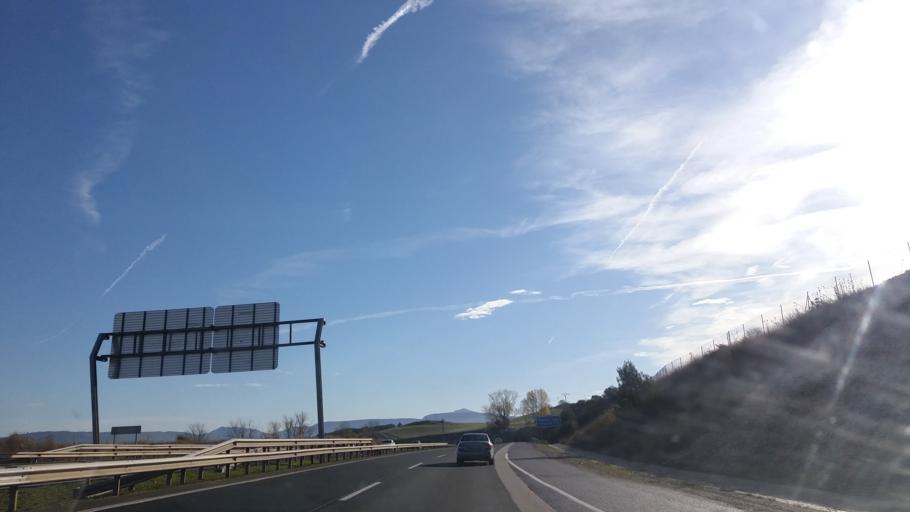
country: ES
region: Navarre
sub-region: Provincia de Navarra
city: Cizur Mayor
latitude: 42.7923
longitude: -1.6791
